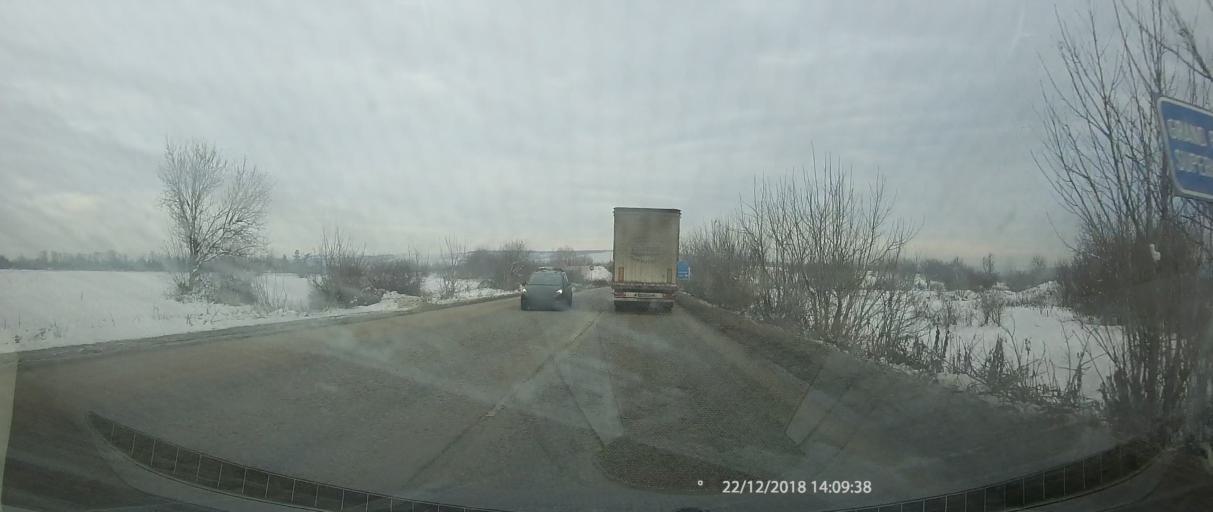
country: BG
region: Pleven
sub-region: Obshtina Dolna Mitropoliya
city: Dolna Mitropoliya
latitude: 43.4385
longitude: 24.5222
